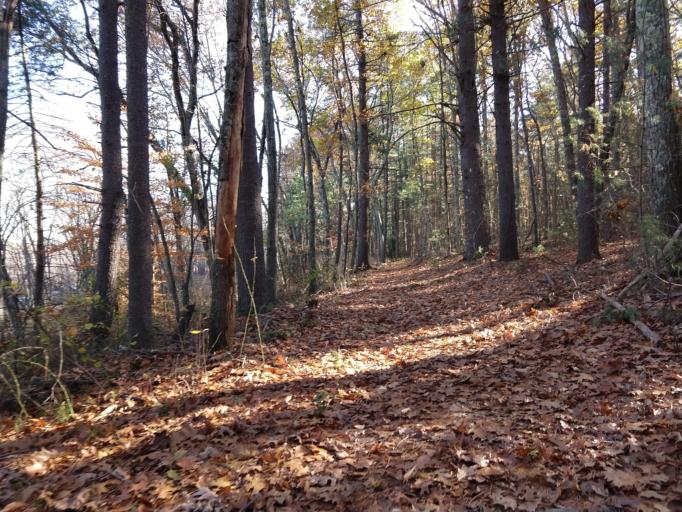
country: US
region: Massachusetts
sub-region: Middlesex County
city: Concord
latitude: 42.4862
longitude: -71.3212
